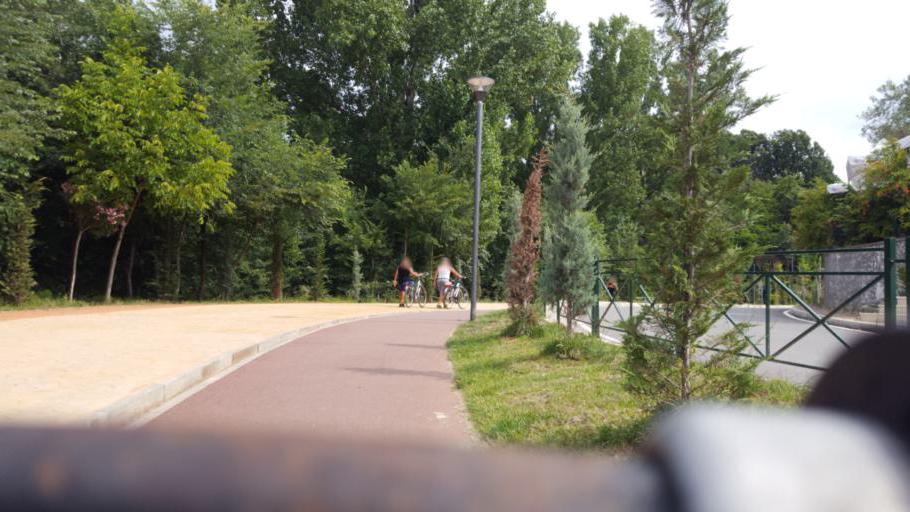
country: AL
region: Tirane
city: Tirana
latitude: 41.3064
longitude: 19.8261
